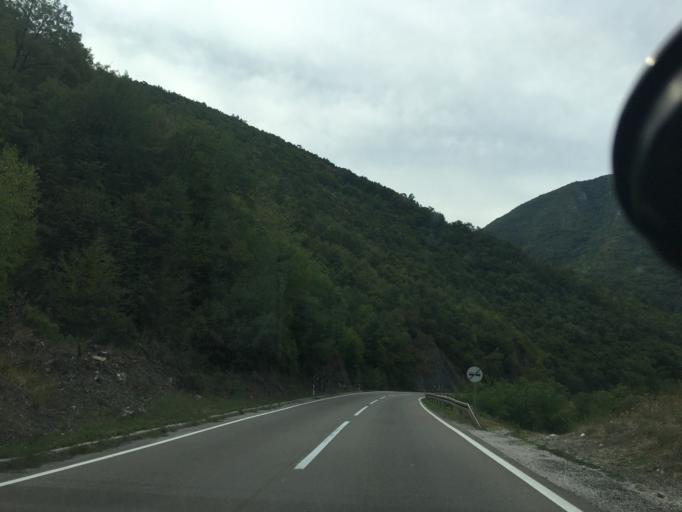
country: RS
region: Central Serbia
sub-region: Moravicki Okrug
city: Lucani
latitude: 43.9136
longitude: 20.2226
